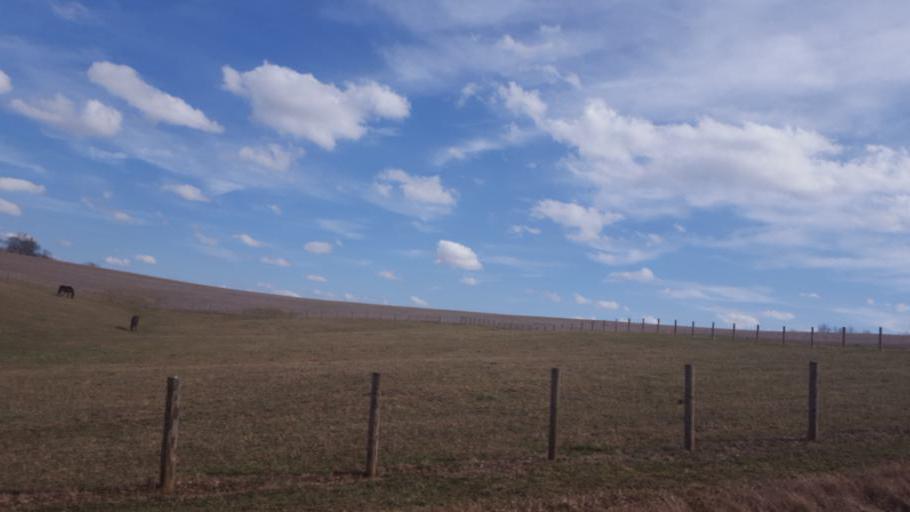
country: US
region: Ohio
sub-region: Knox County
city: Gambier
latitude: 40.4466
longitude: -82.3903
